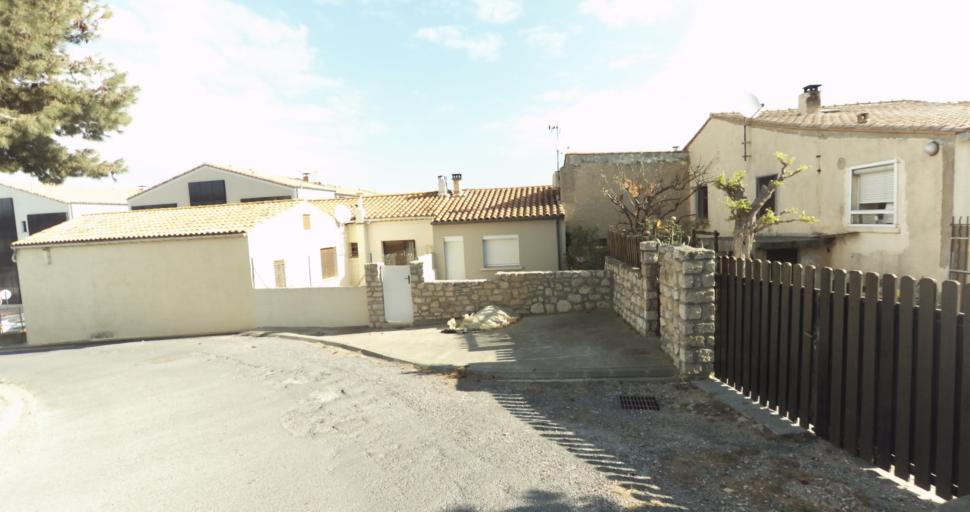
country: FR
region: Languedoc-Roussillon
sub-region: Departement de l'Aude
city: Leucate
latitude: 42.9102
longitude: 3.0251
